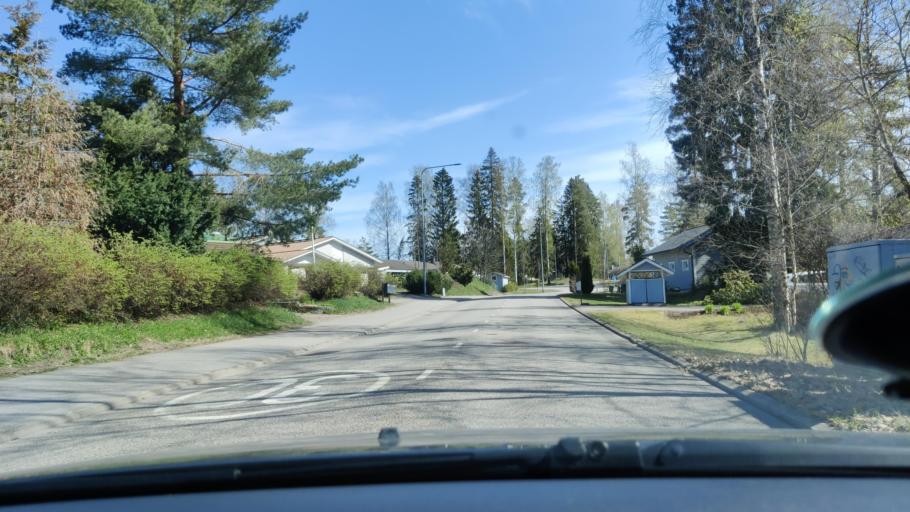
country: FI
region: Uusimaa
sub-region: Helsinki
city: Kerava
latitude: 60.3618
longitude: 25.0921
